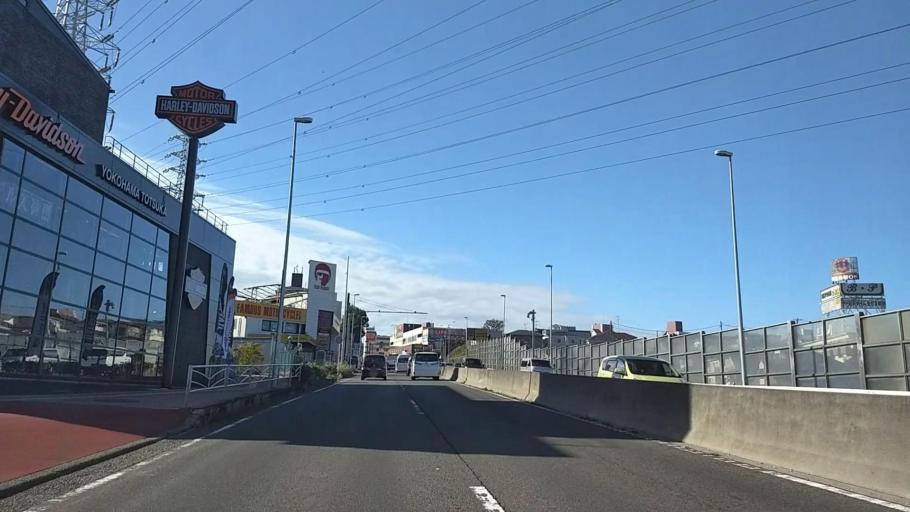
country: JP
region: Kanagawa
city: Fujisawa
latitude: 35.3922
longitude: 139.5234
